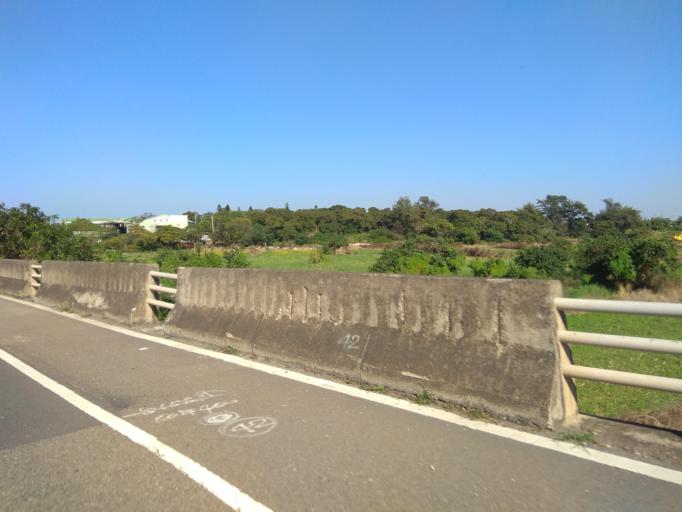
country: TW
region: Taiwan
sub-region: Hsinchu
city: Zhubei
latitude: 24.9957
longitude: 121.0350
